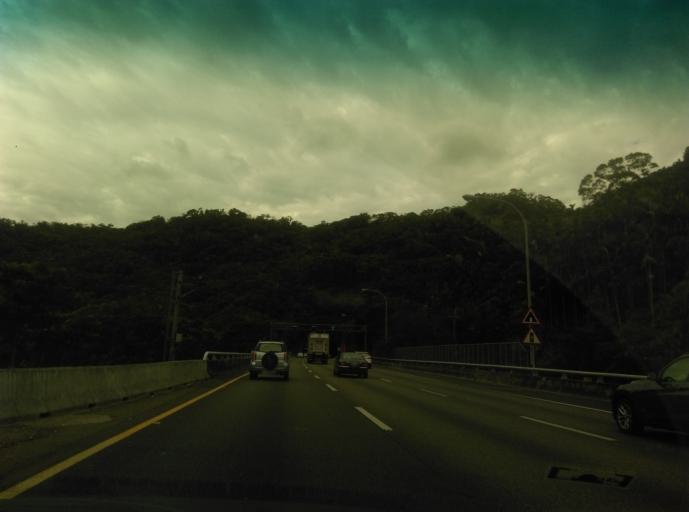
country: TW
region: Taipei
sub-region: Taipei
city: Banqiao
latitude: 24.9797
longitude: 121.5002
